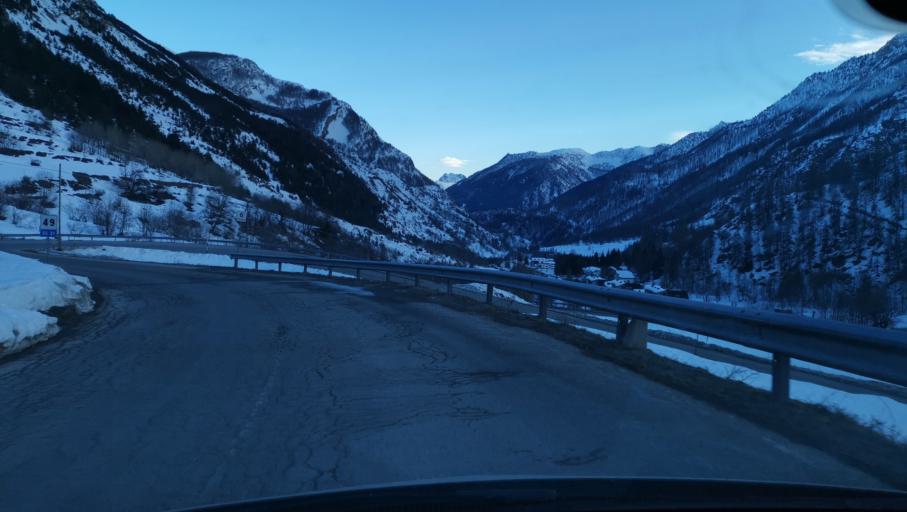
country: IT
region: Piedmont
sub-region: Provincia di Cuneo
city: Bersezio
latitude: 44.3743
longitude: 6.9756
